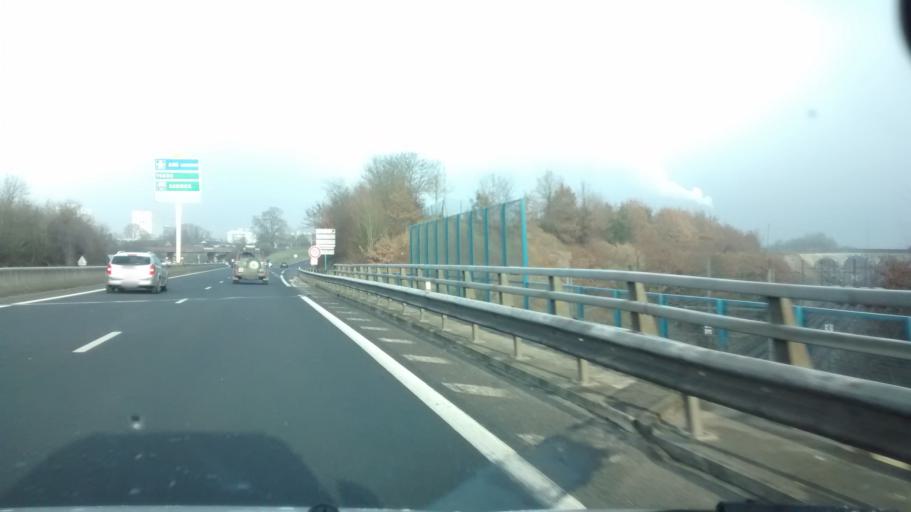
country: FR
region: Centre
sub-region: Departement d'Indre-et-Loire
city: Joue-les-Tours
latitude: 47.3371
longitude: 0.6696
